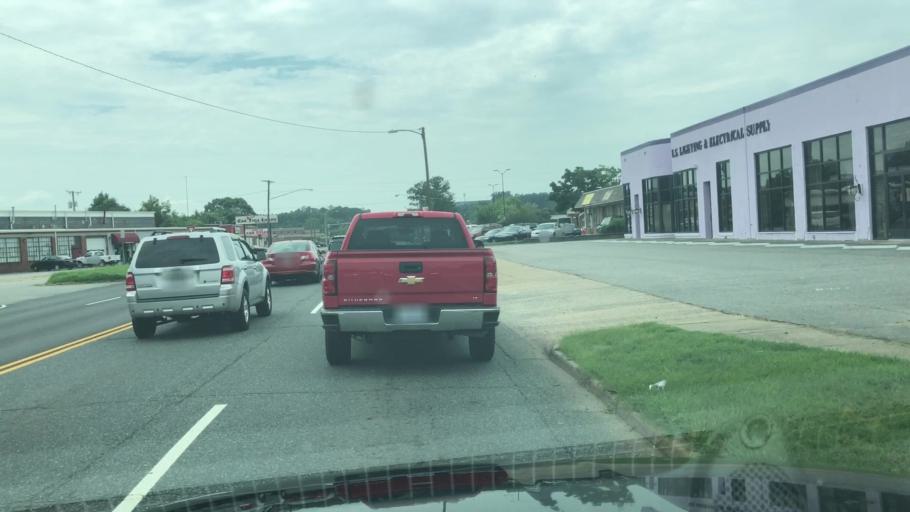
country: US
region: Virginia
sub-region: Stafford County
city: Falmouth
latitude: 38.3162
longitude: -77.4727
